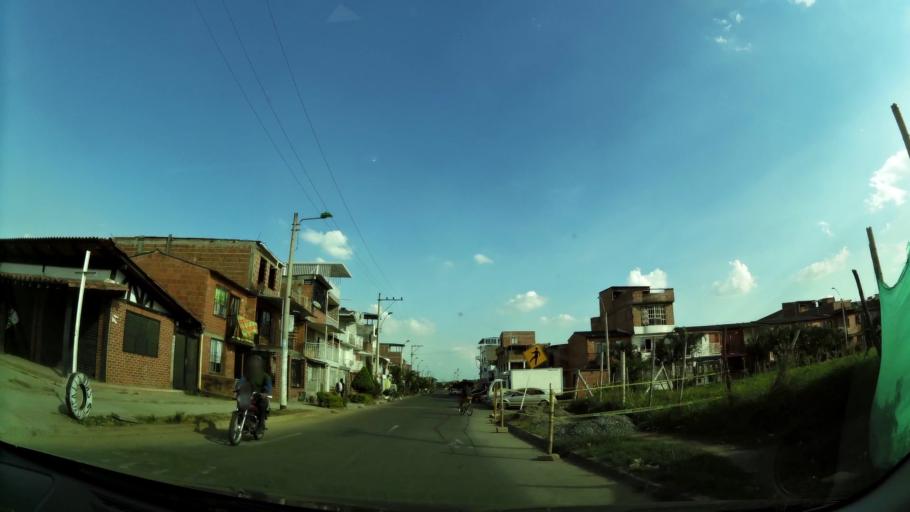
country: CO
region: Valle del Cauca
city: Cali
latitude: 3.3948
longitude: -76.5119
